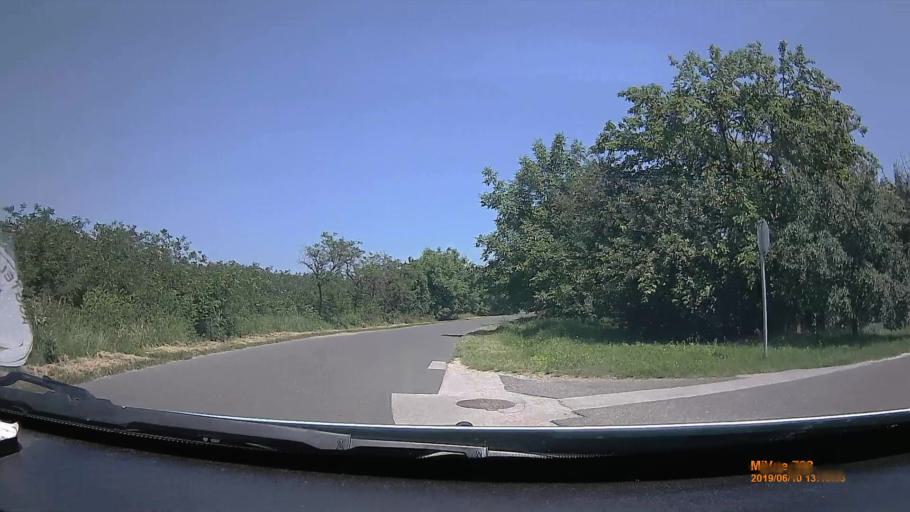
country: HU
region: Borsod-Abauj-Zemplen
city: Tiszaluc
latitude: 48.0397
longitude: 21.0701
